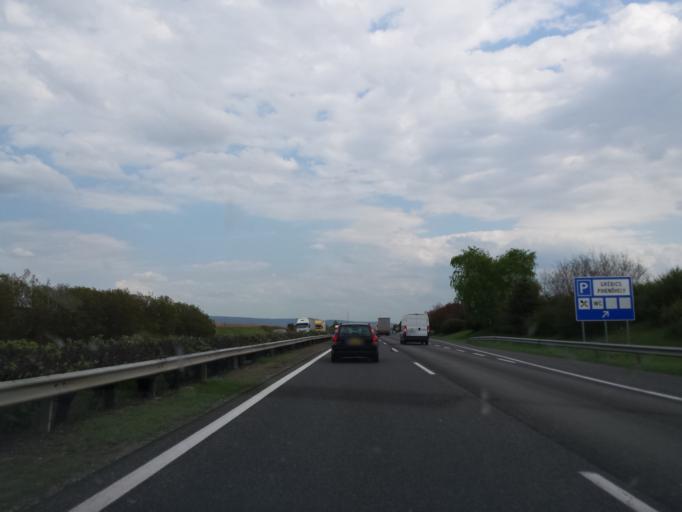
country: HU
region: Komarom-Esztergom
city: Kocs
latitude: 47.6367
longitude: 18.2355
